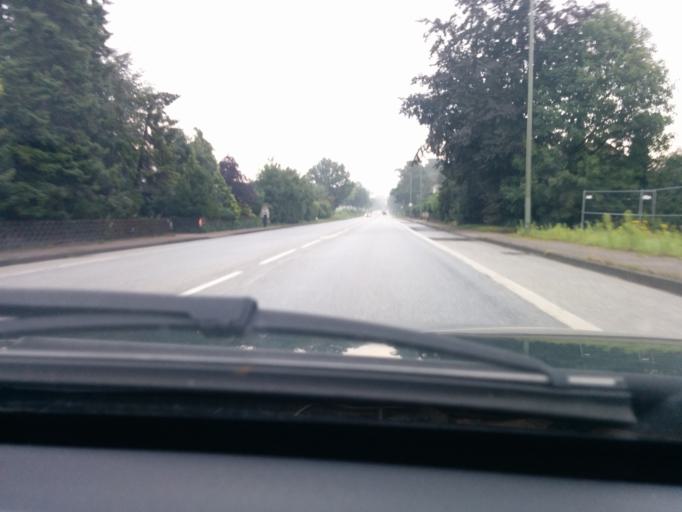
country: DE
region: North Rhine-Westphalia
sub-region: Regierungsbezirk Detmold
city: Bielefeld
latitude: 52.0062
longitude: 8.4785
